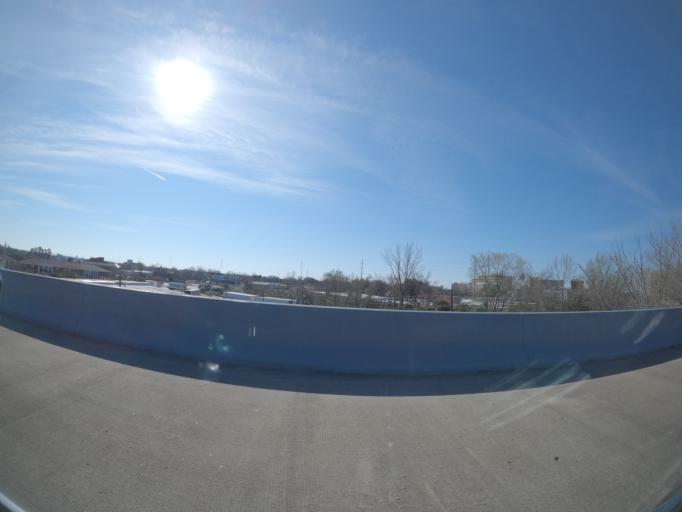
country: US
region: Georgia
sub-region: Richmond County
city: Augusta
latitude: 33.4762
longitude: -81.9796
